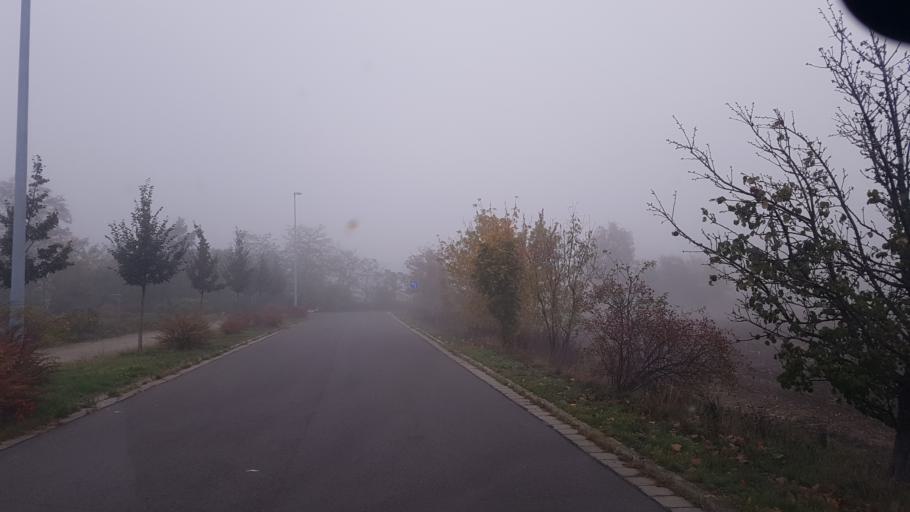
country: DE
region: Brandenburg
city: Elsterwerda
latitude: 51.4659
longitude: 13.5414
